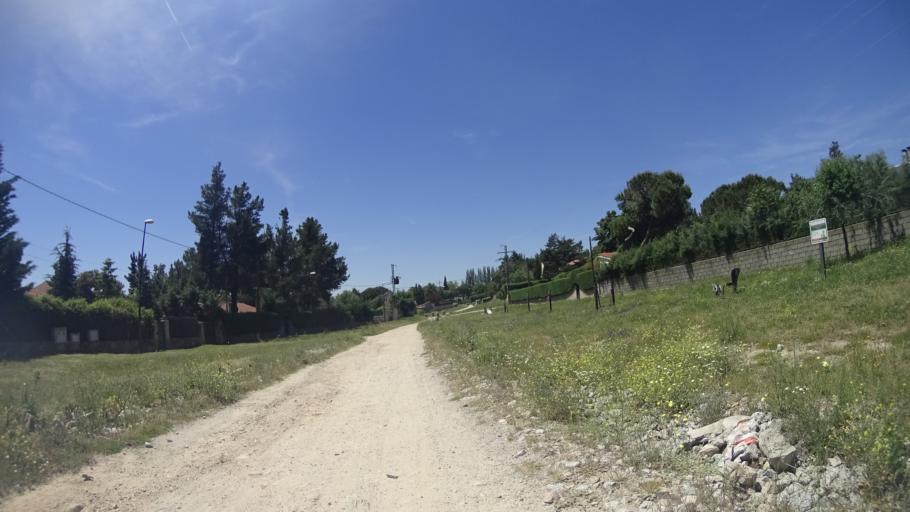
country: ES
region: Madrid
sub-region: Provincia de Madrid
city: Navalquejigo
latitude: 40.6197
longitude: -4.0334
